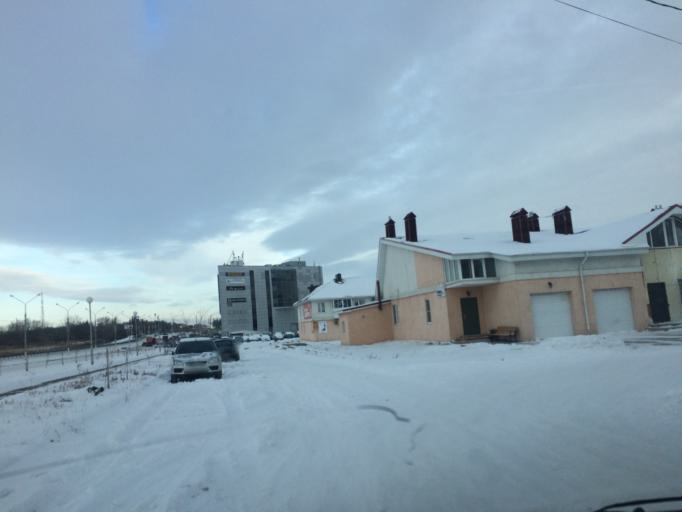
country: RU
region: Chelyabinsk
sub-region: Gorod Magnitogorsk
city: Magnitogorsk
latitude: 53.3849
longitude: 58.9622
